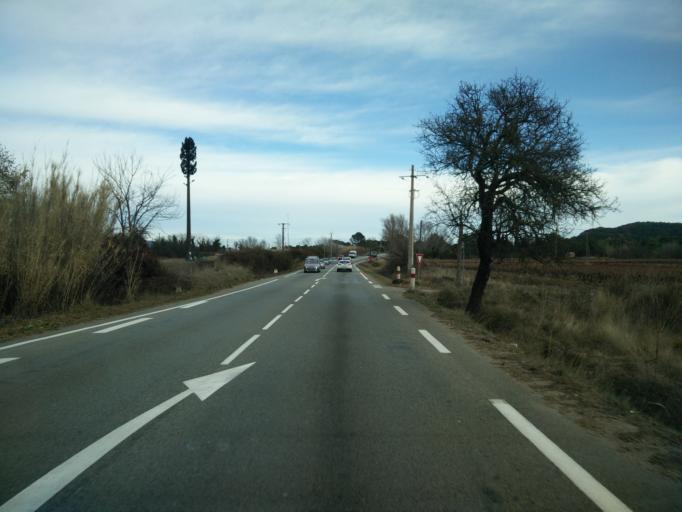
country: FR
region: Provence-Alpes-Cote d'Azur
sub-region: Departement du Var
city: Les Arcs
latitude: 43.4531
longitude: 6.5055
